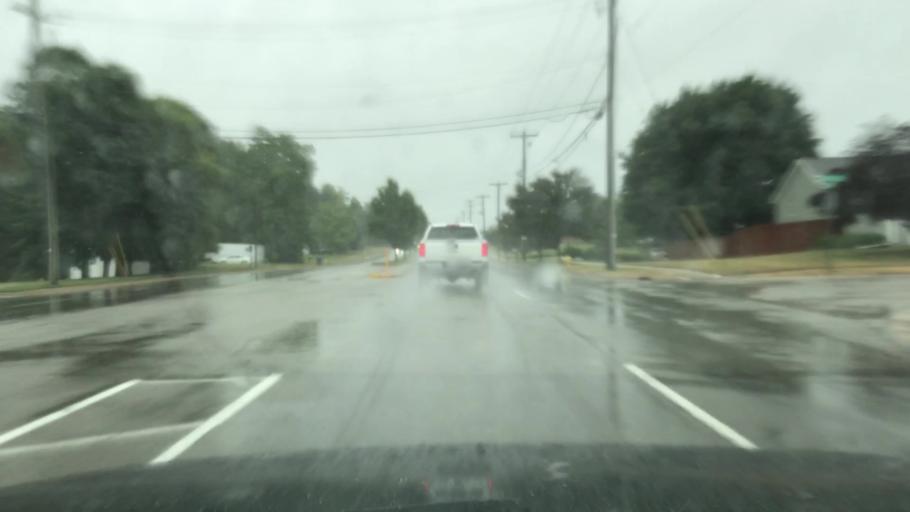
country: US
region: Michigan
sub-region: Kent County
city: Wyoming
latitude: 42.8679
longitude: -85.7234
